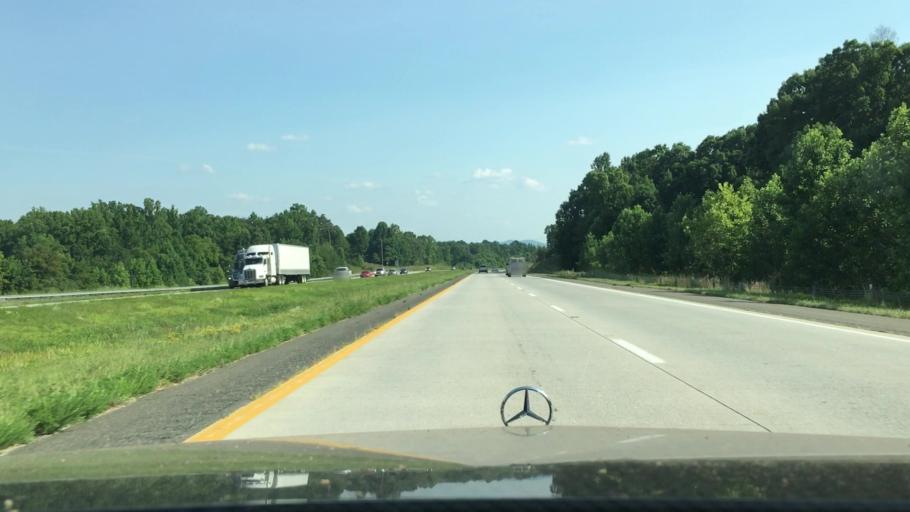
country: US
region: Virginia
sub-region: Amherst County
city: Madison Heights
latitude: 37.4408
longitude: -79.0765
